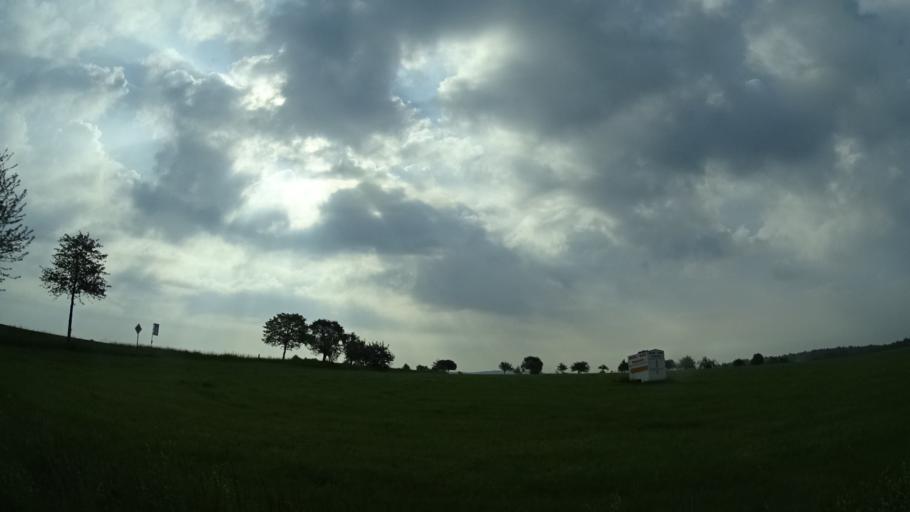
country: DE
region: Hesse
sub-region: Regierungsbezirk Darmstadt
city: Lutzelbach
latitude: 49.7143
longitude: 9.0869
